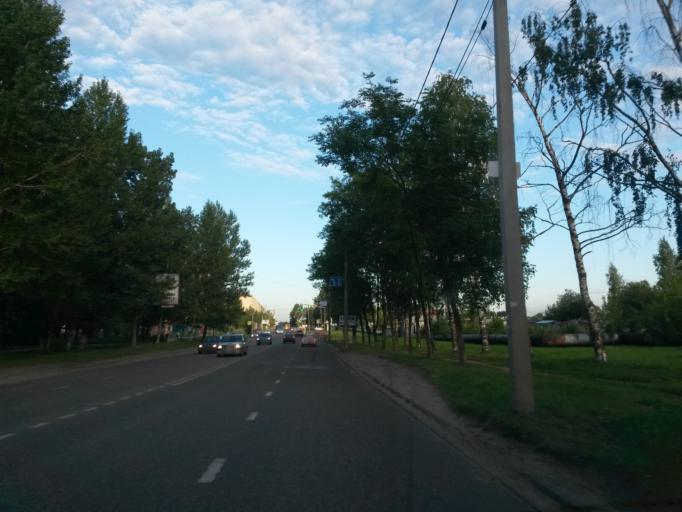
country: RU
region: Jaroslavl
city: Yaroslavl
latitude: 57.5714
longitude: 39.8565
